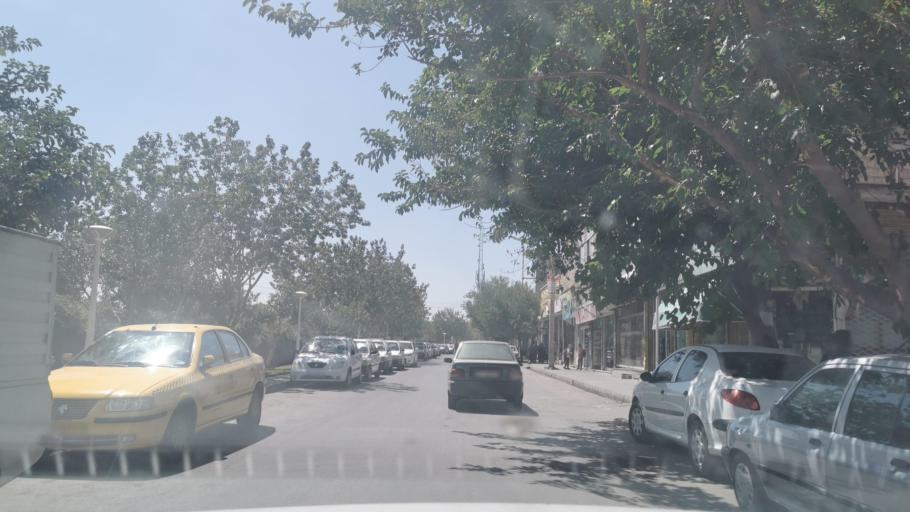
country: IR
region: Razavi Khorasan
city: Mashhad
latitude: 36.3605
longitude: 59.5535
